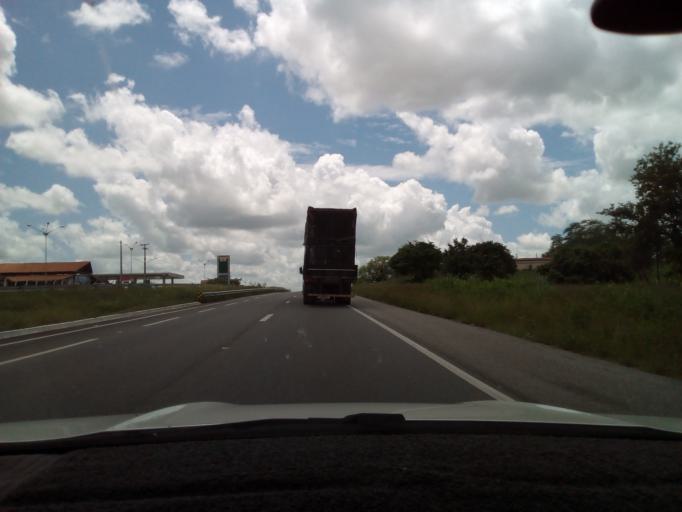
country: BR
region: Paraiba
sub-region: Gurinhem
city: Gurinhem
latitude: -7.1691
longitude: -35.3733
